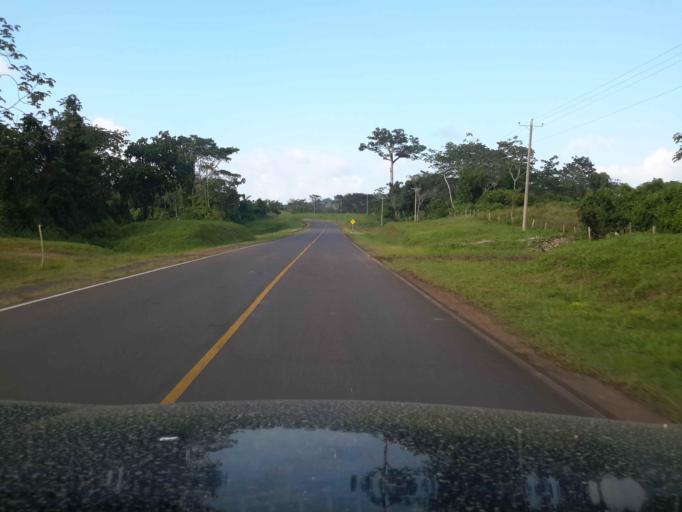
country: NI
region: Rio San Juan
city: San Carlos
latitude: 11.1824
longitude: -84.6782
